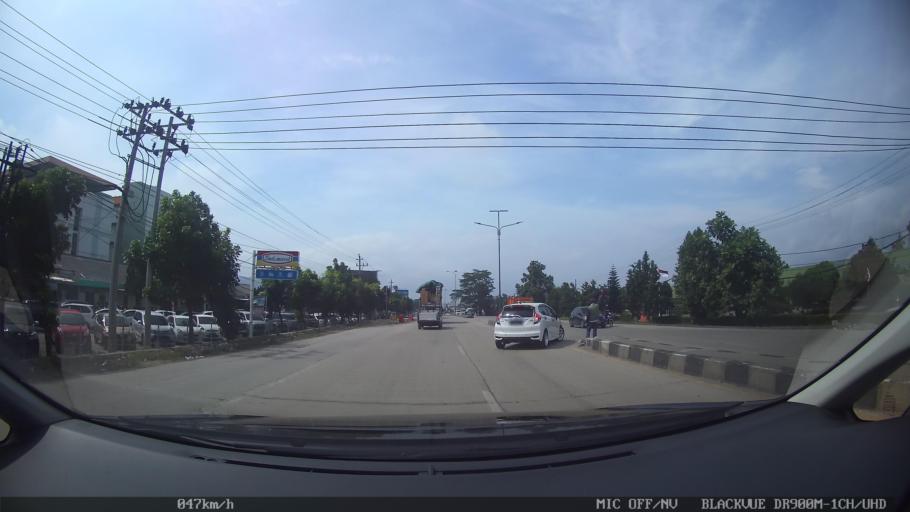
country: ID
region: Lampung
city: Kedaton
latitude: -5.3853
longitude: 105.2871
